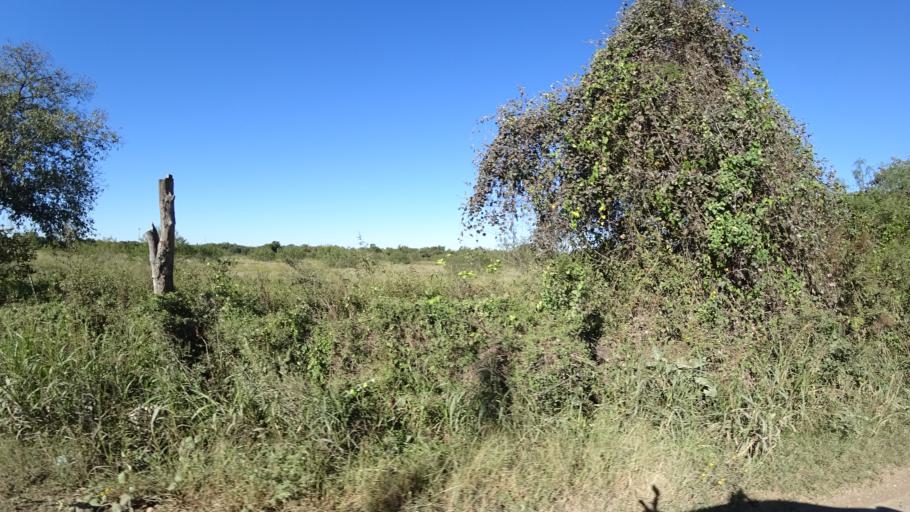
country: US
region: Texas
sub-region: Travis County
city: Austin
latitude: 30.2448
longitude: -97.6802
